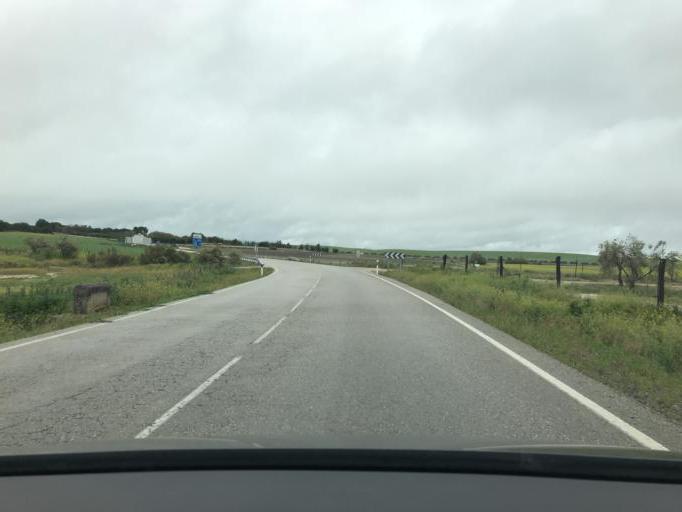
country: ES
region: Andalusia
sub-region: Provincia de Sevilla
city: Paradas
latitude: 37.2684
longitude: -5.4476
